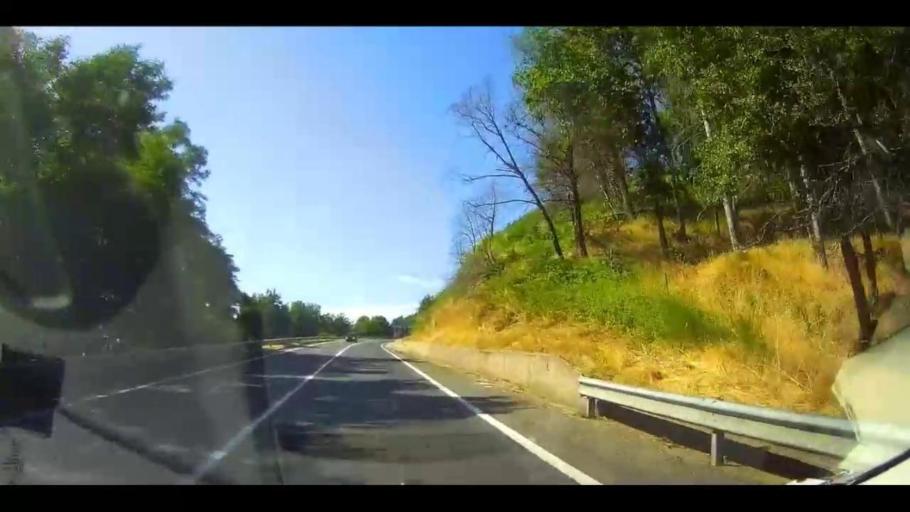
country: IT
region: Calabria
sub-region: Provincia di Cosenza
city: Celico
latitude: 39.3228
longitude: 16.3648
